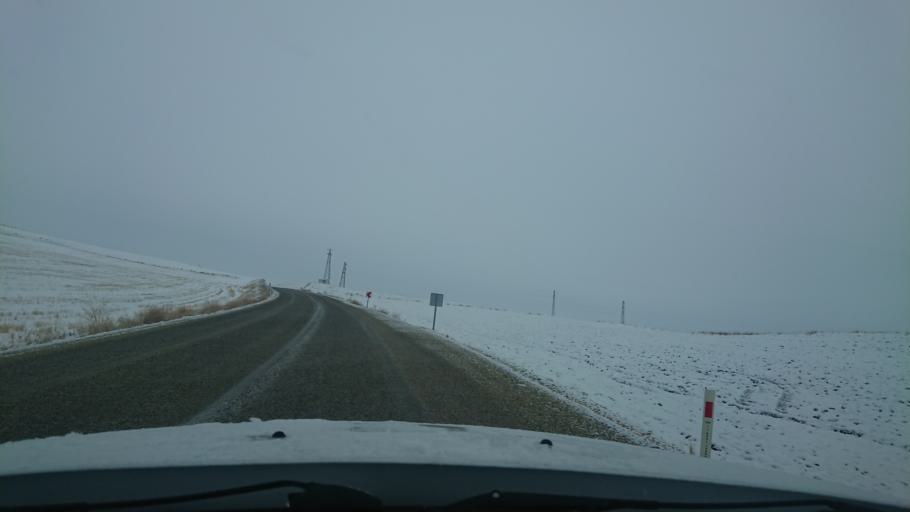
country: TR
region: Aksaray
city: Agacoren
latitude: 38.7641
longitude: 33.8714
